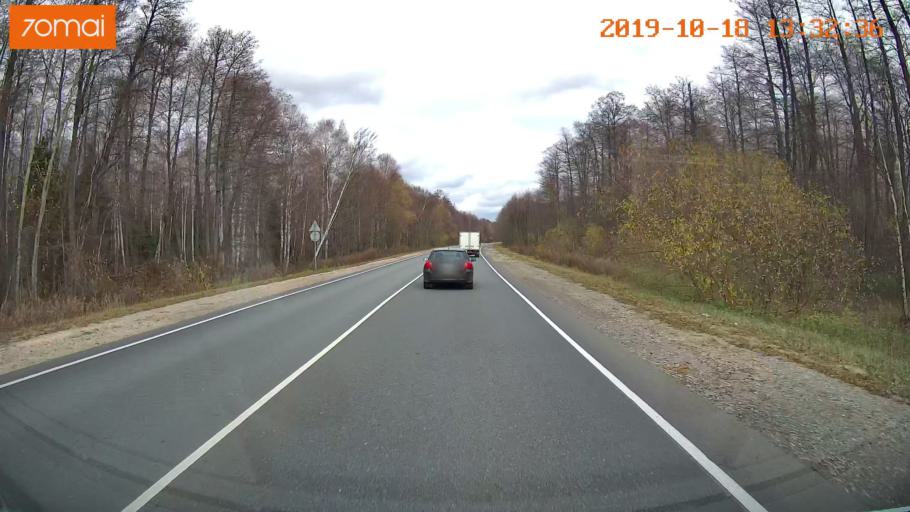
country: RU
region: Rjazan
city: Solotcha
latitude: 54.8351
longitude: 39.9208
